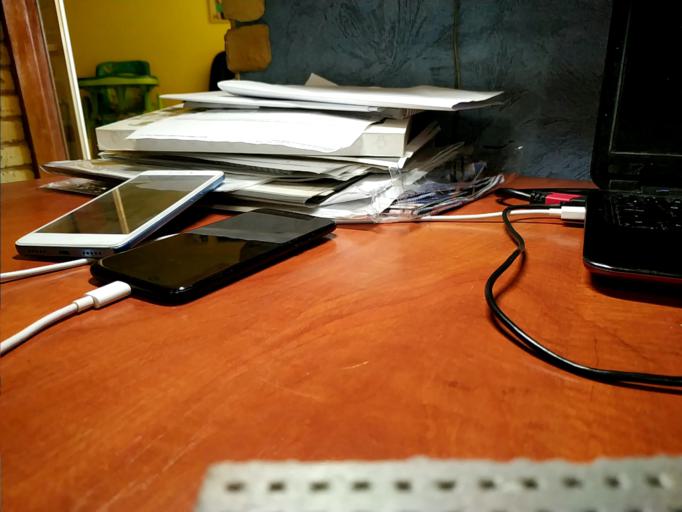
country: RU
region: Tverskaya
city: Kalashnikovo
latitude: 57.4062
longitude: 35.1954
